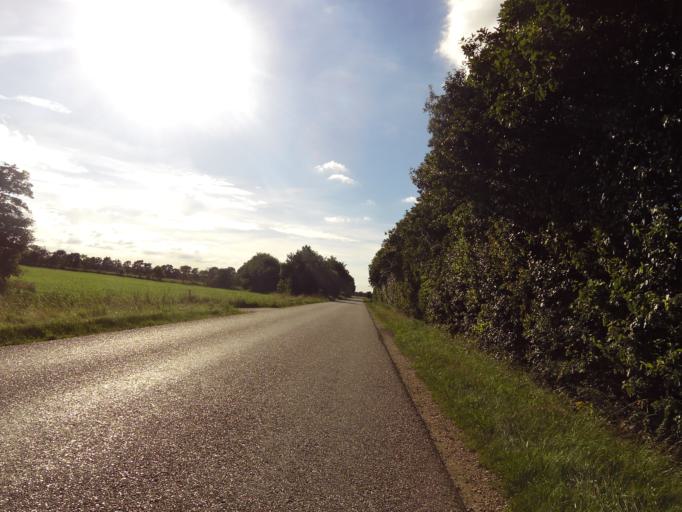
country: DK
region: South Denmark
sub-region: Haderslev Kommune
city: Vojens
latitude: 55.2041
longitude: 9.2795
